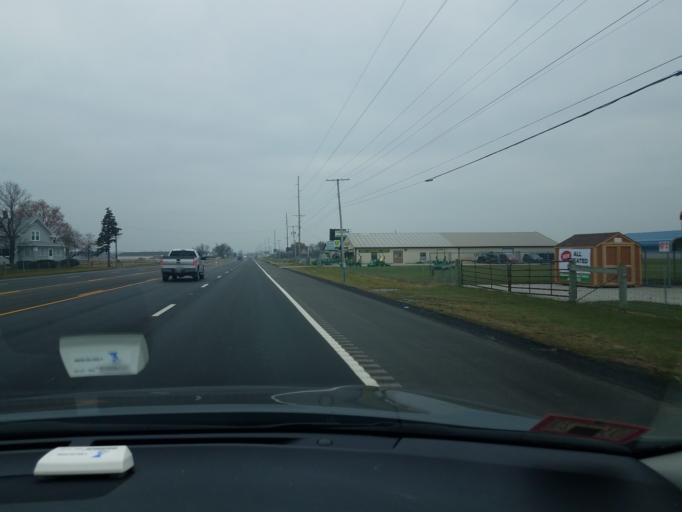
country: US
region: Ohio
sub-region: Erie County
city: Milan
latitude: 41.3534
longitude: -82.6336
